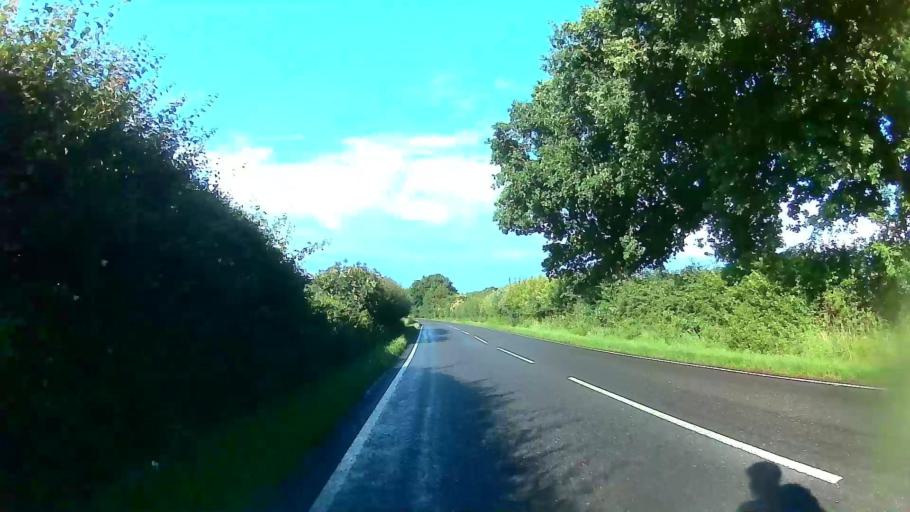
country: GB
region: England
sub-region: Essex
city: Writtle
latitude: 51.7165
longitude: 0.3955
